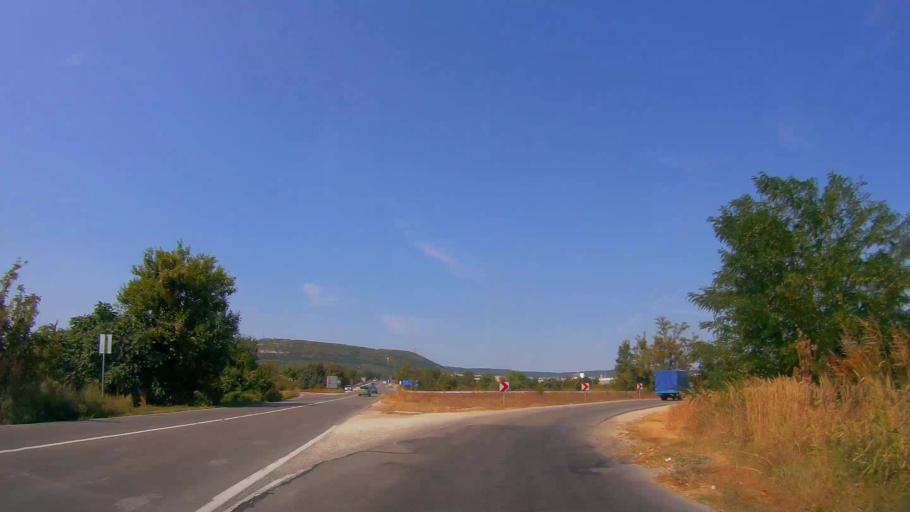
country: BG
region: Shumen
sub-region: Obshtina Shumen
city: Shumen
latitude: 43.2470
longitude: 26.9692
